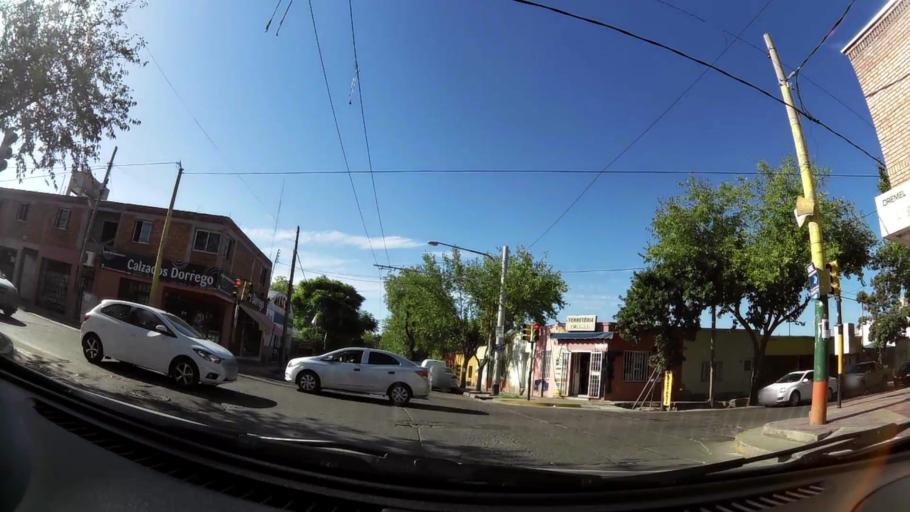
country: AR
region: Mendoza
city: Mendoza
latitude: -32.9033
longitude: -68.8304
